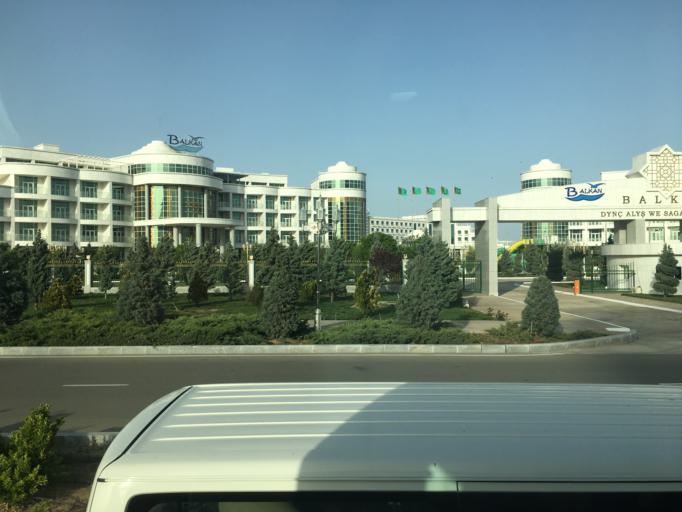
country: TM
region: Balkan
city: Turkmenbasy
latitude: 39.9807
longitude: 52.8268
